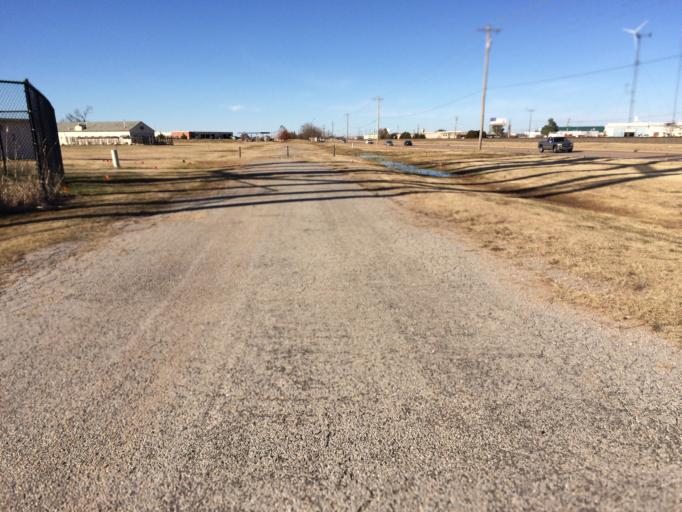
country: US
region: Oklahoma
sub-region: Cleveland County
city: Norman
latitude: 35.2412
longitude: -97.4573
